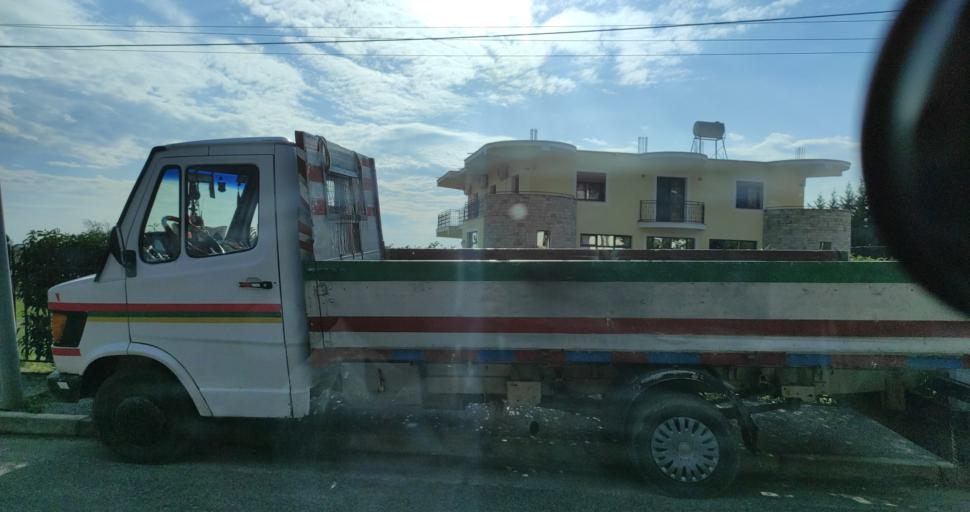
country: AL
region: Lezhe
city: Lezhe
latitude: 41.7961
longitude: 19.6200
